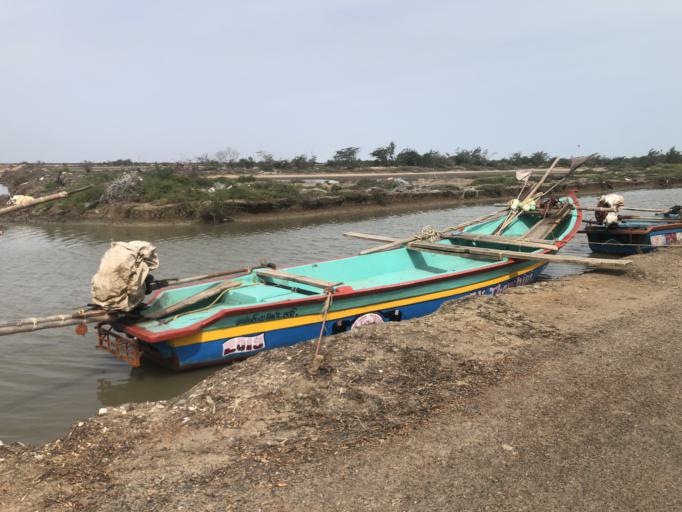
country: IN
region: Tamil Nadu
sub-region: Thanjavur
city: Adirampattinam
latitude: 10.3202
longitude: 79.3800
